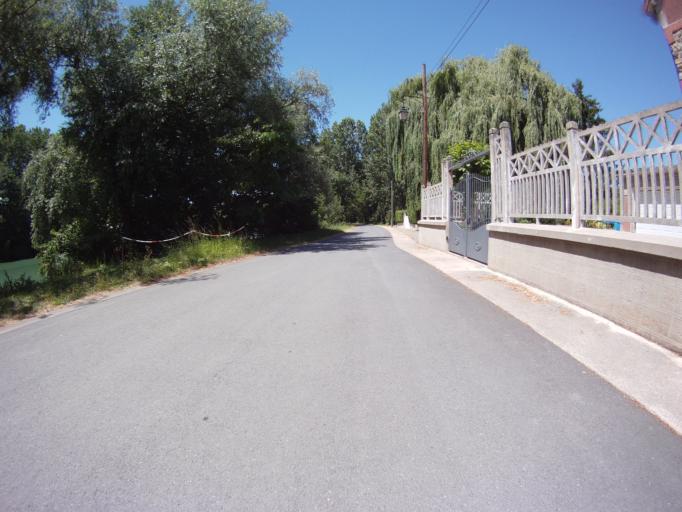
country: FR
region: Champagne-Ardenne
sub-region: Departement de la Marne
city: Mardeuil
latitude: 49.0712
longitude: 3.9433
